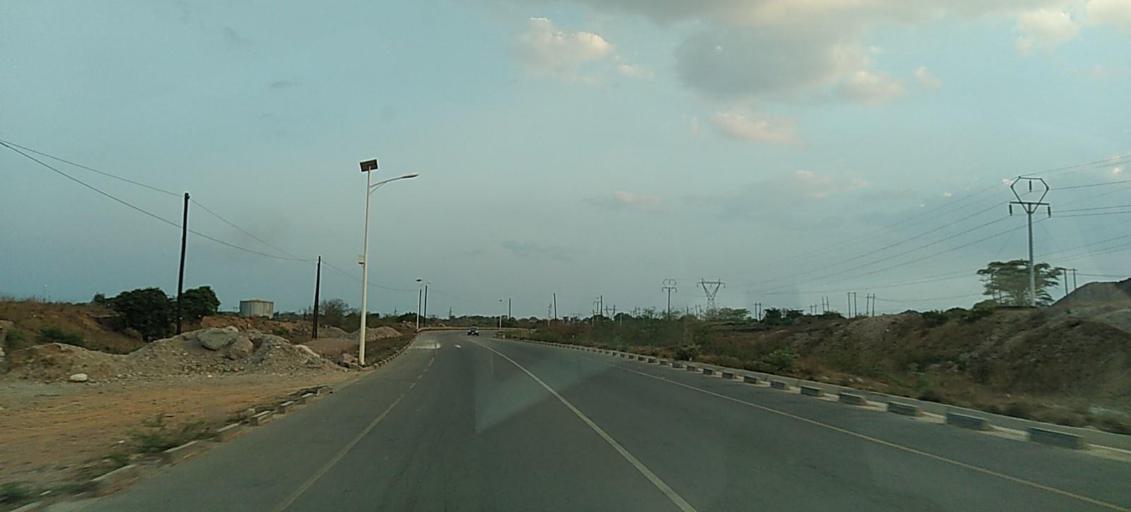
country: ZM
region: Copperbelt
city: Chingola
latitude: -12.5313
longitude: 27.8368
